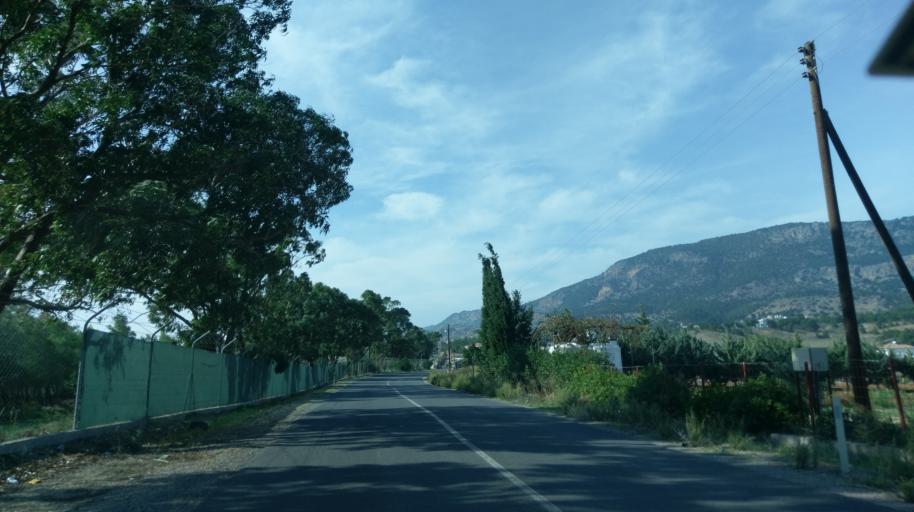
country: CY
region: Keryneia
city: Kyrenia
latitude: 35.2801
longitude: 33.2684
